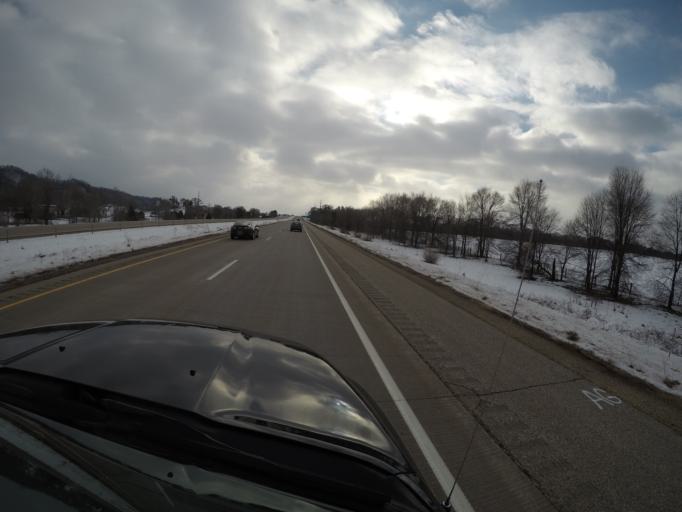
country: US
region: Wisconsin
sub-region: La Crosse County
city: Holmen
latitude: 44.0053
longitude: -91.2865
